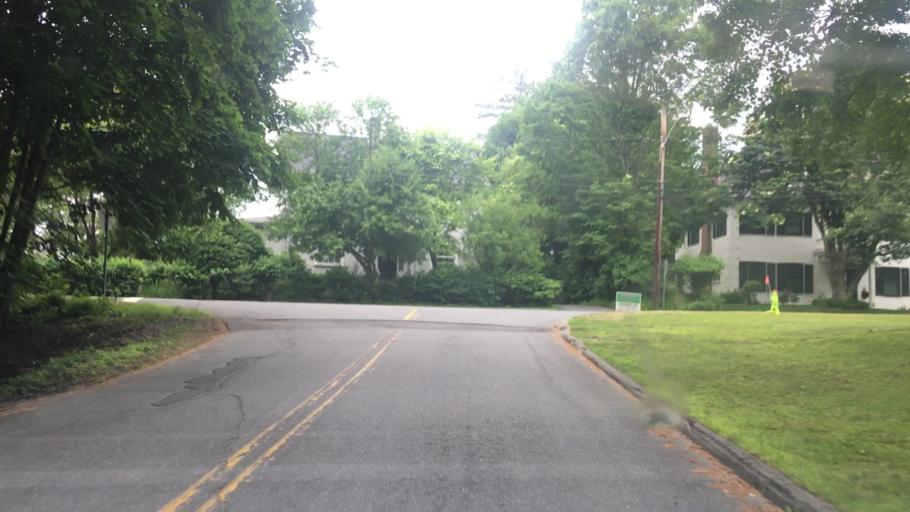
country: US
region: New Hampshire
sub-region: Grafton County
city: Hanover
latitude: 43.6982
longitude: -72.2911
